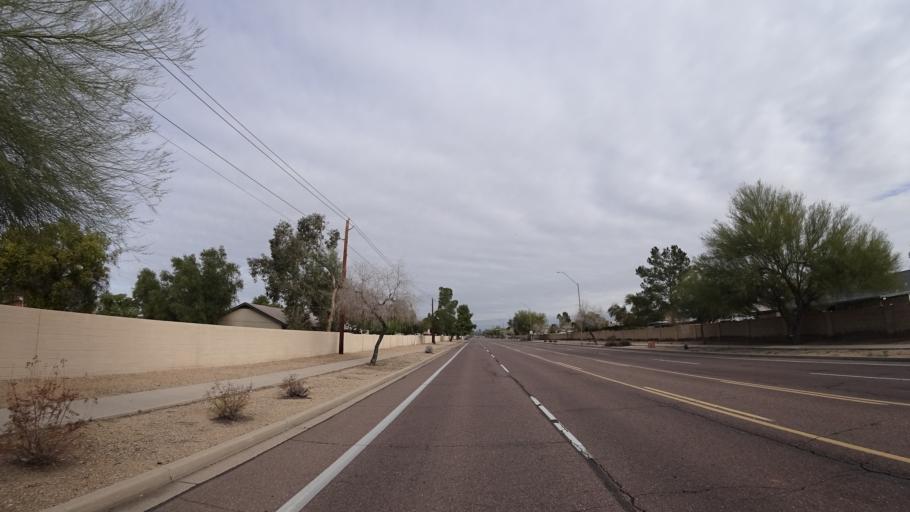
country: US
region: Arizona
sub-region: Maricopa County
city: Peoria
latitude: 33.6450
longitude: -112.1520
